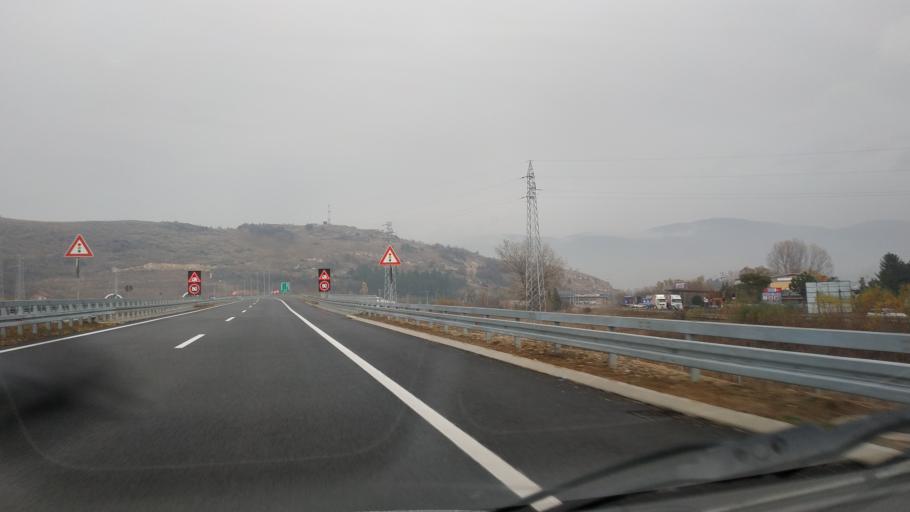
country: RS
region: Central Serbia
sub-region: Pirotski Okrug
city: Pirot
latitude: 43.1558
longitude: 22.5726
